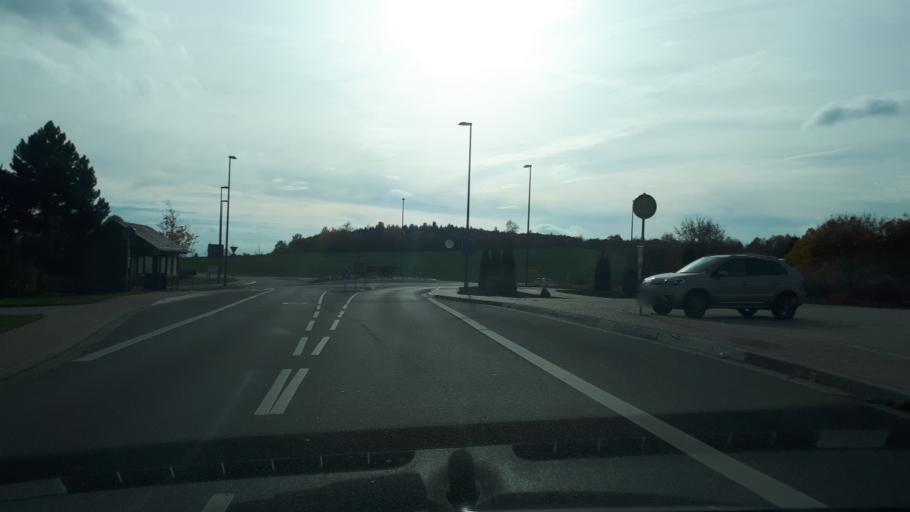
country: DE
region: Rheinland-Pfalz
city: Laubach
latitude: 50.2320
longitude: 7.0720
